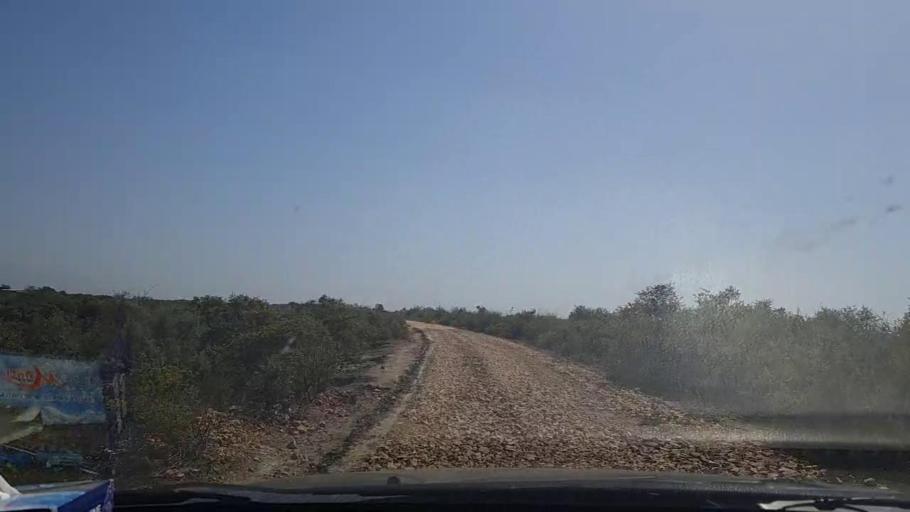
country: PK
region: Sindh
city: Chuhar Jamali
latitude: 24.2723
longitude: 67.7461
